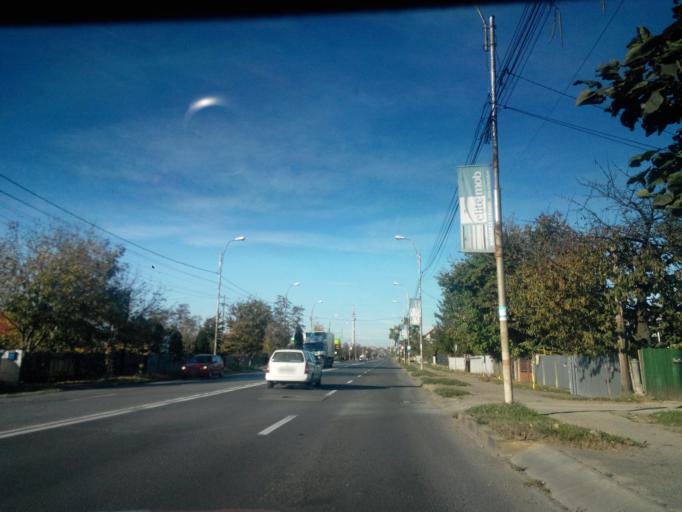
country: RO
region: Bacau
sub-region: Comuna Saucesti
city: Saucesti
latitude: 46.5891
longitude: 26.9304
